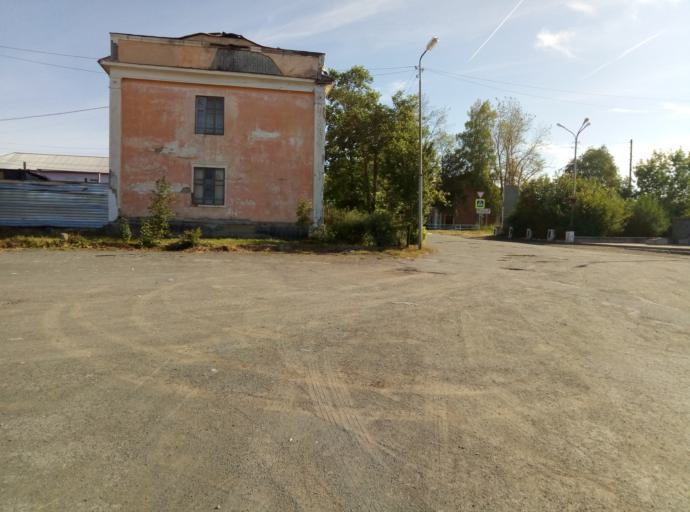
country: RU
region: Sverdlovsk
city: Karpinsk
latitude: 59.7766
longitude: 59.9803
